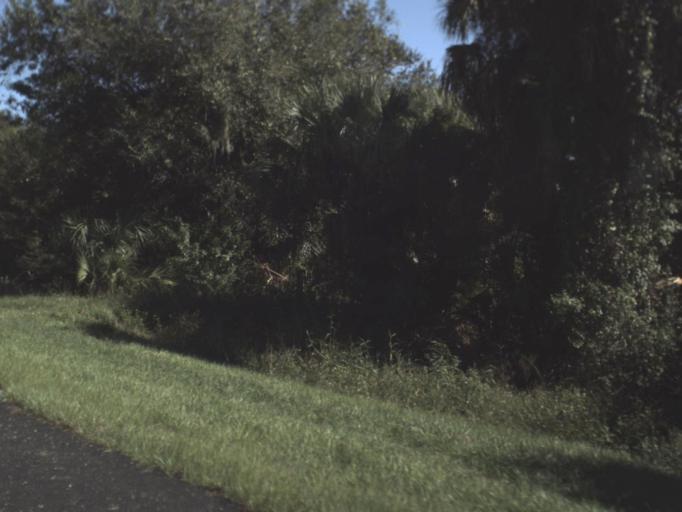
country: US
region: Florida
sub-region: Hendry County
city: Port LaBelle
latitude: 26.7685
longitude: -81.3052
